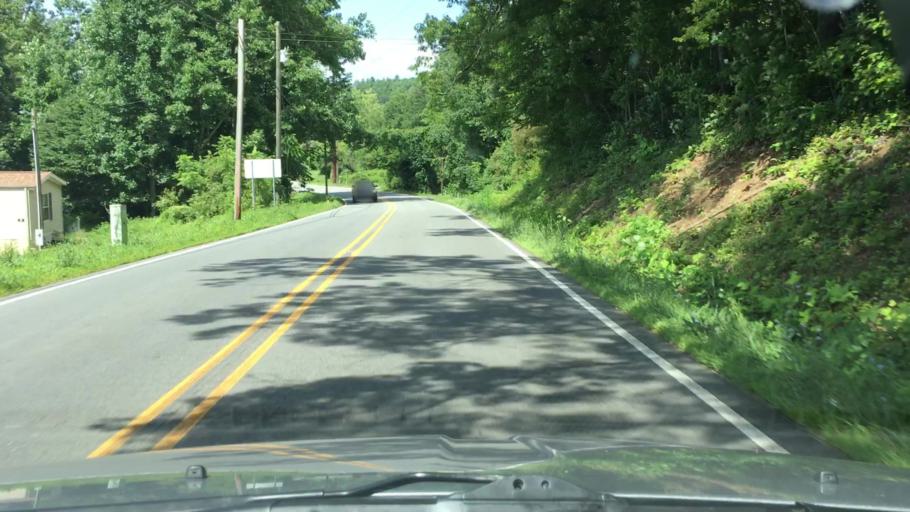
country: US
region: North Carolina
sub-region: Yancey County
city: Burnsville
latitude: 35.8845
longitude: -82.2158
